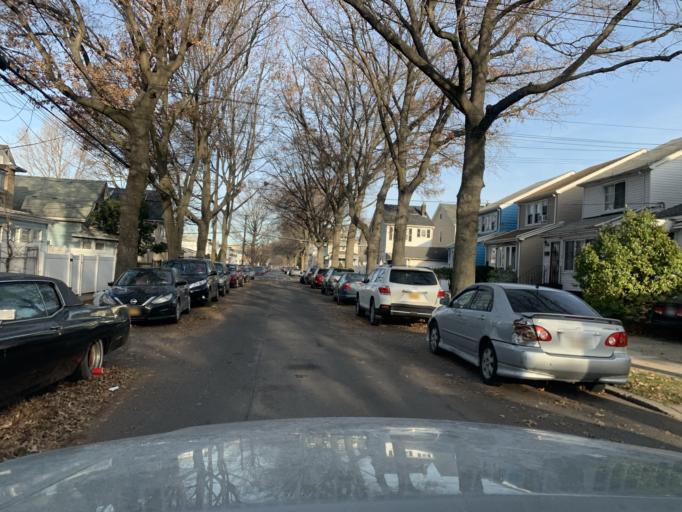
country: US
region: New York
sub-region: Queens County
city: Jamaica
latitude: 40.6890
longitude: -73.7924
